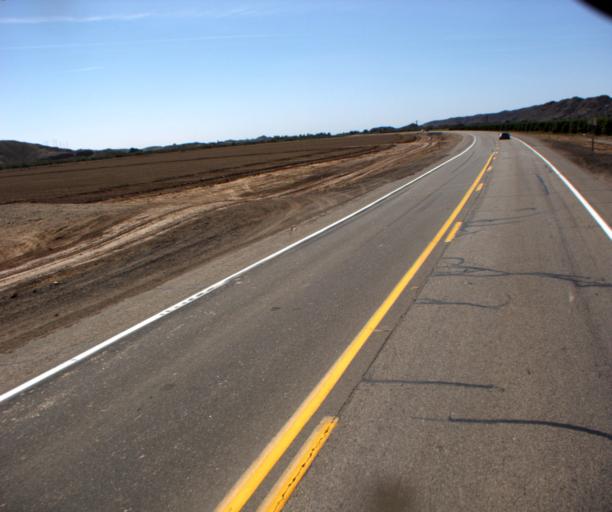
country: US
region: Arizona
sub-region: Yuma County
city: Fortuna Foothills
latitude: 32.7681
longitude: -114.4011
